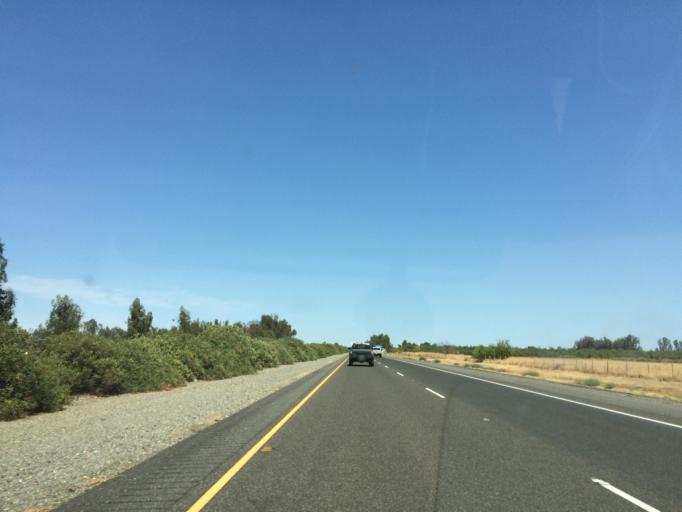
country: US
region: California
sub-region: Glenn County
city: Orland
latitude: 39.7258
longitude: -122.2059
